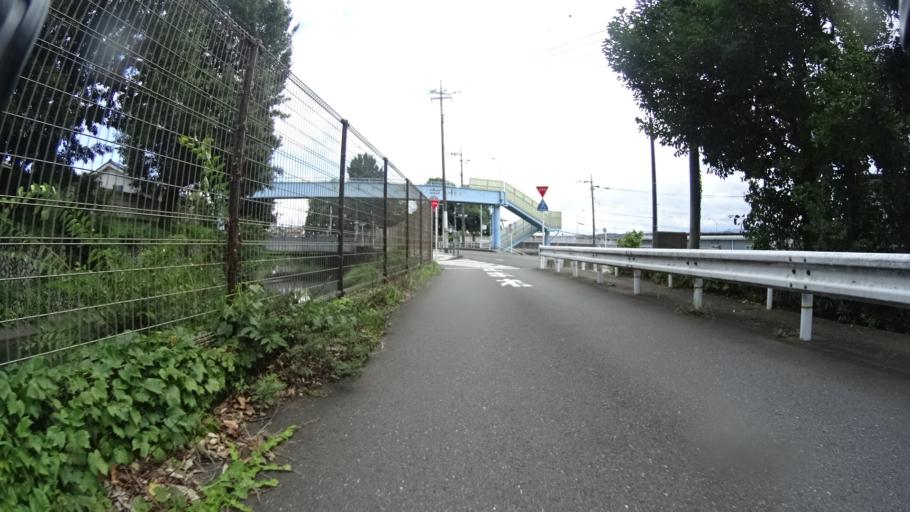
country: JP
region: Tokyo
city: Fussa
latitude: 35.7363
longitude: 139.3262
